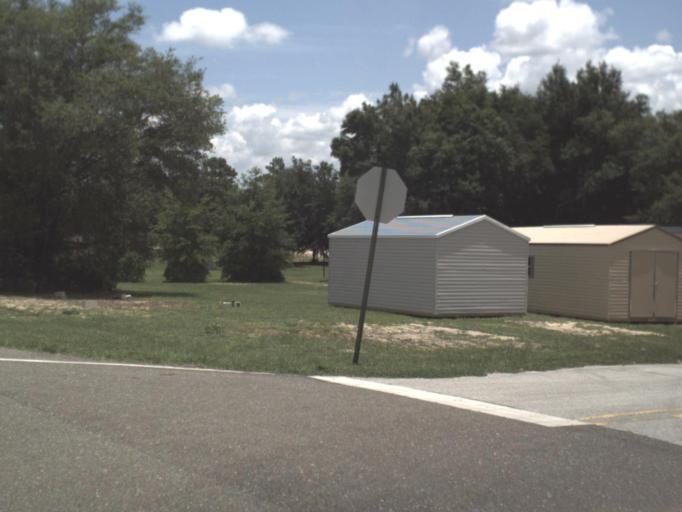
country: US
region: Florida
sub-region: Levy County
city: East Bronson
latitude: 29.4717
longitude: -82.6115
